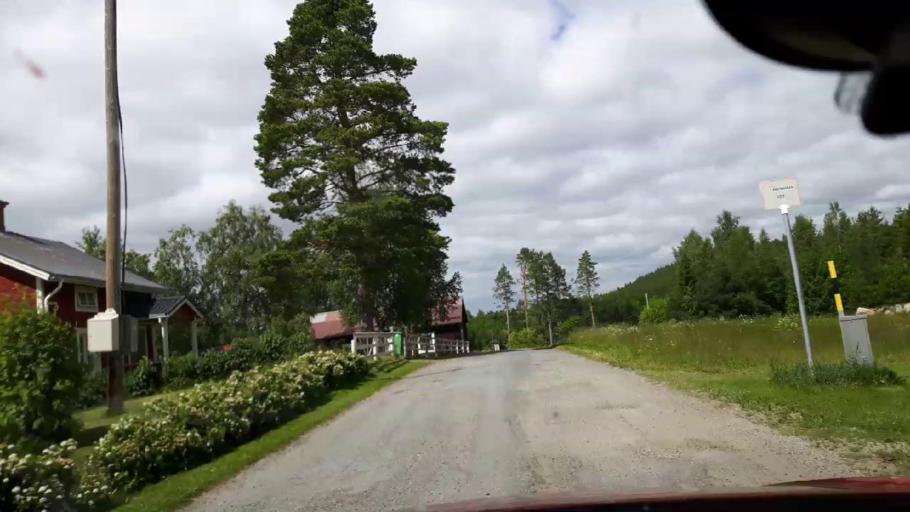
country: SE
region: Jaemtland
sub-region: Braecke Kommun
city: Braecke
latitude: 62.8534
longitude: 15.2910
